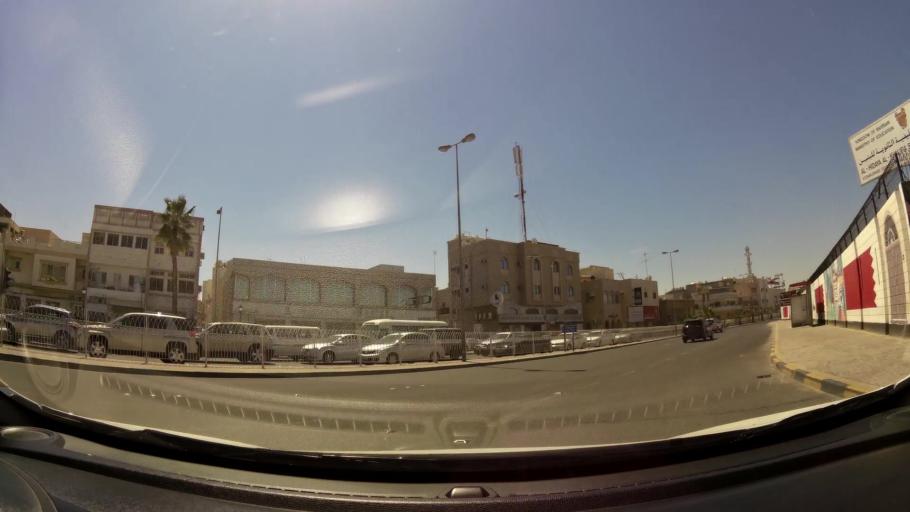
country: BH
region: Muharraq
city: Al Muharraq
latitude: 26.2616
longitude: 50.6103
